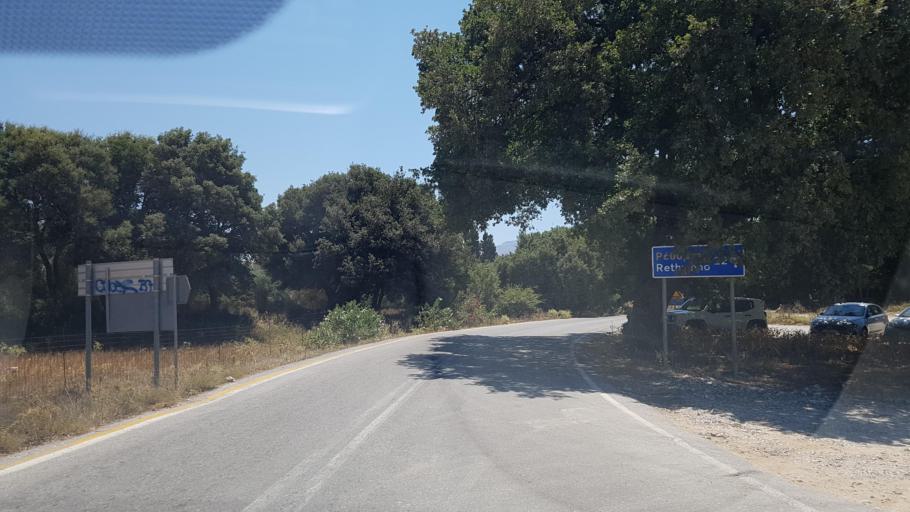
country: GR
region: Crete
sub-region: Nomos Rethymnis
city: Agia Foteini
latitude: 35.3081
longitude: 24.6291
